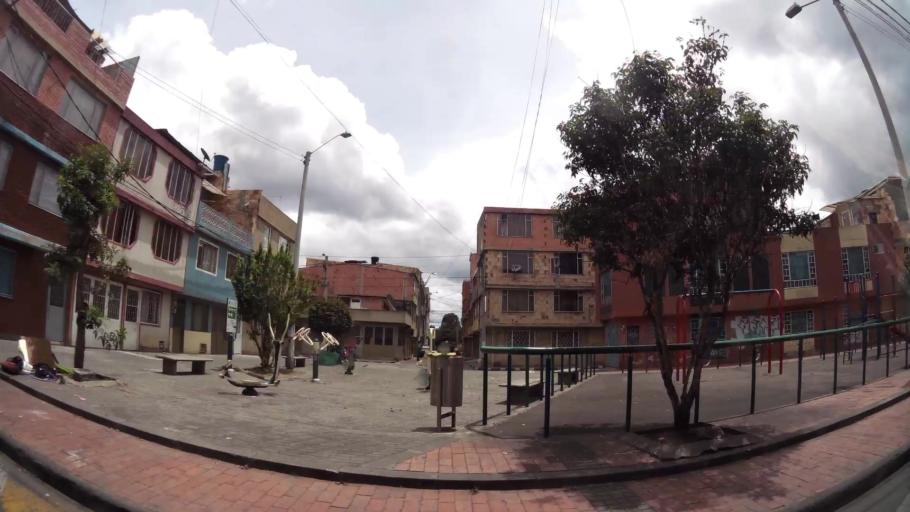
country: CO
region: Cundinamarca
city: Funza
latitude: 4.6995
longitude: -74.1236
